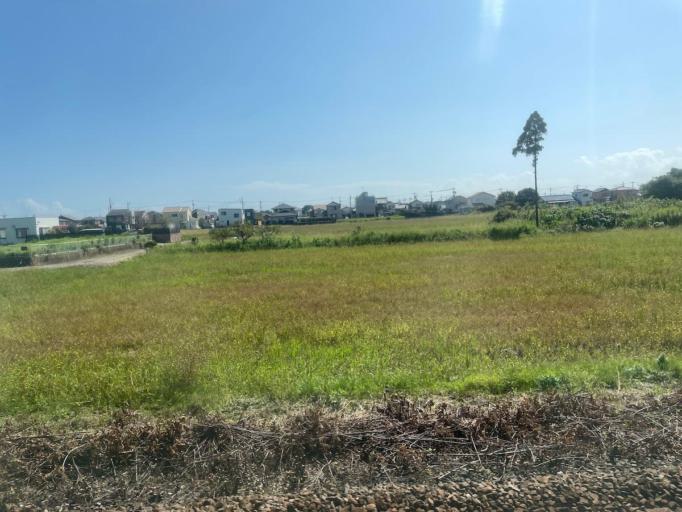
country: JP
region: Mie
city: Kawage
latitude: 34.8107
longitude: 136.5672
